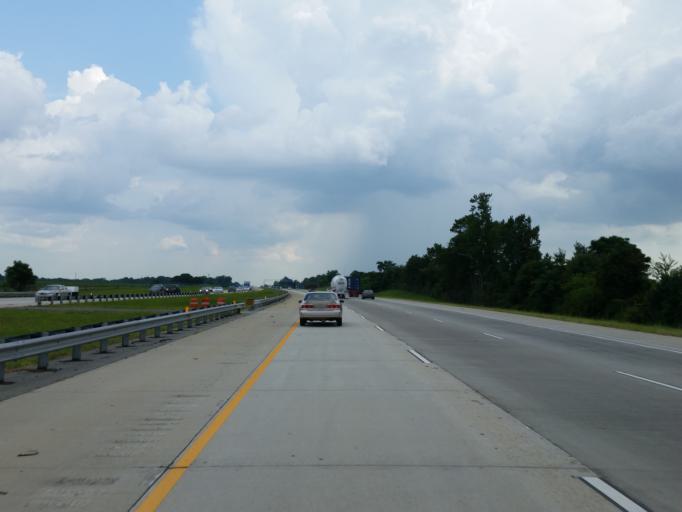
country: US
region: Georgia
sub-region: Dooly County
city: Unadilla
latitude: 32.2182
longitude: -83.7449
